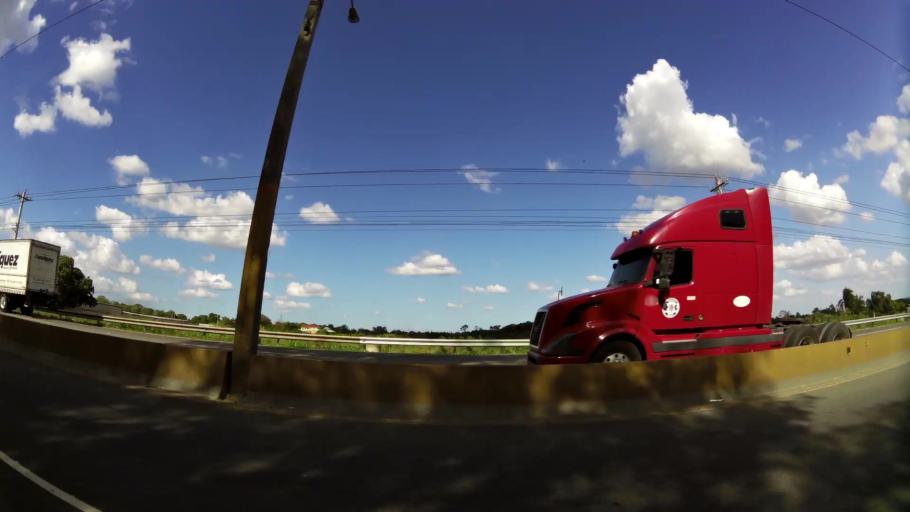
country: DO
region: Santo Domingo
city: Santo Domingo Oeste
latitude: 18.5436
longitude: -70.0363
